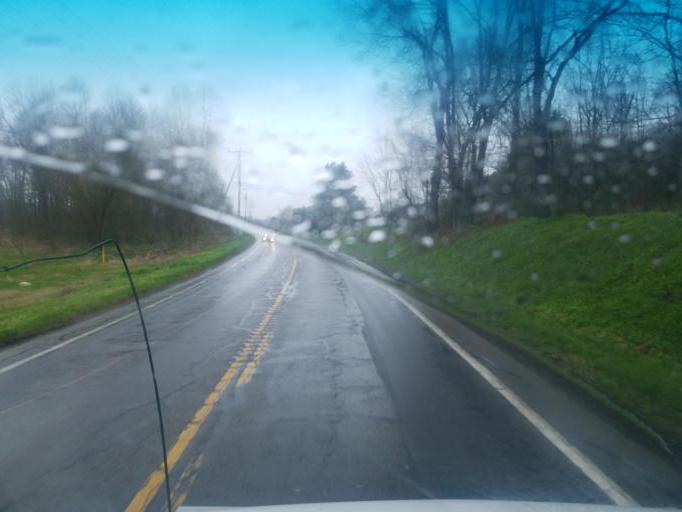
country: US
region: Ohio
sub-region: Holmes County
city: Millersburg
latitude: 40.6036
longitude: -81.9131
